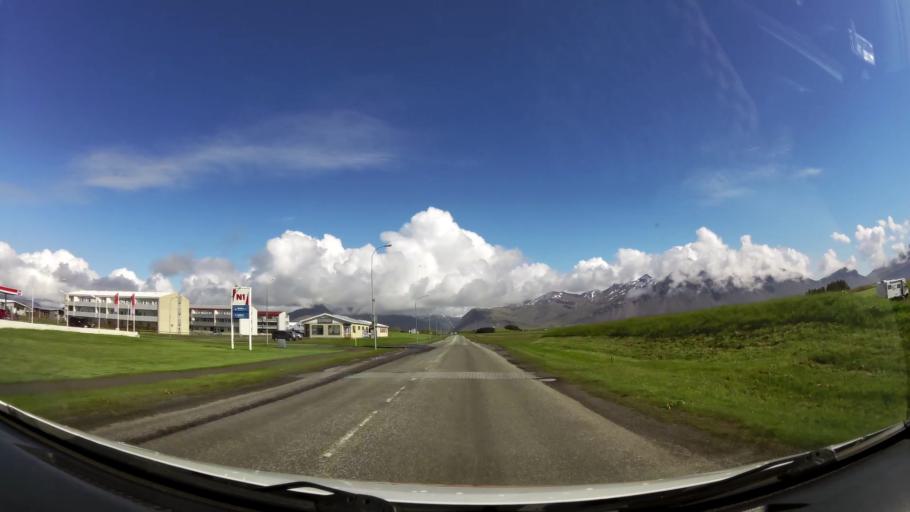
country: IS
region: East
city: Hoefn
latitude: 64.2586
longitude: -15.2049
